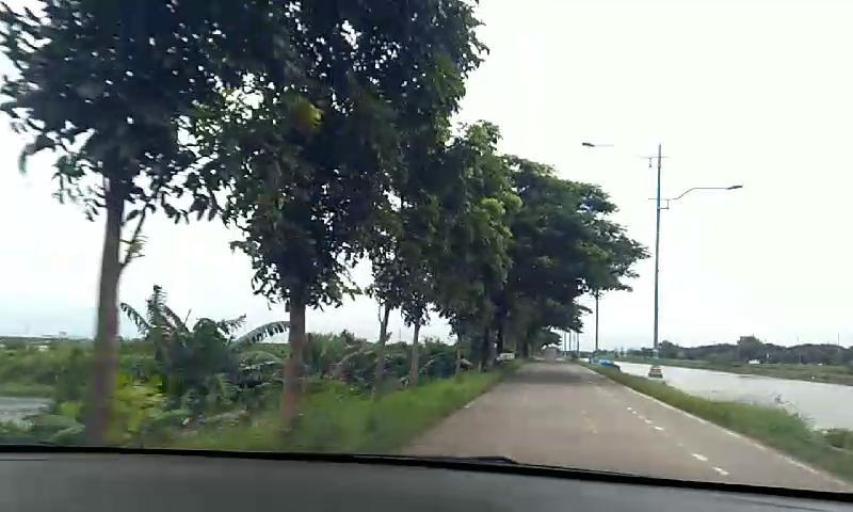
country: ID
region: West Java
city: Bekasi
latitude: -6.1290
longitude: 106.9691
